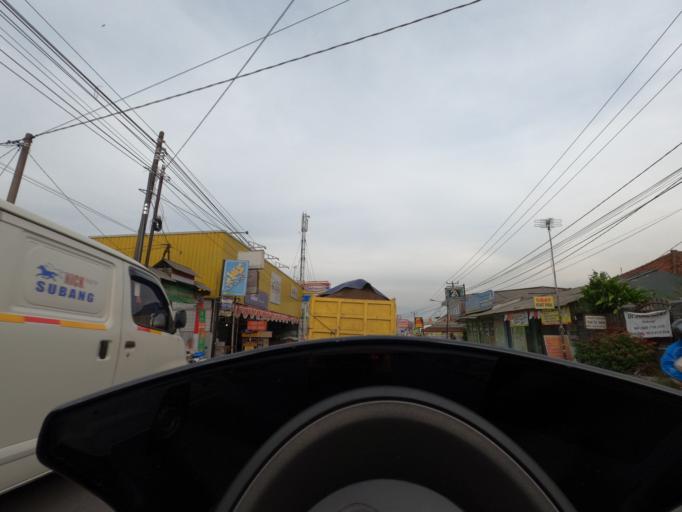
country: ID
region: West Java
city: Lembang
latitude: -6.6777
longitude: 107.6842
